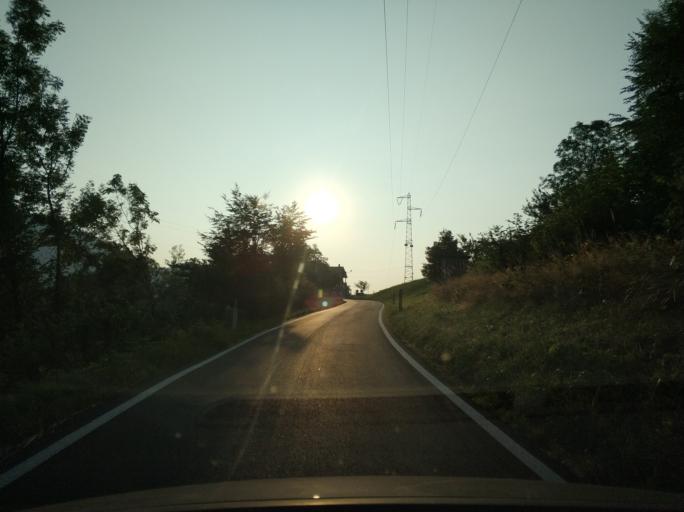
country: IT
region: Piedmont
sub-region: Provincia di Torino
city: Viu
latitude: 45.2302
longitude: 7.3739
